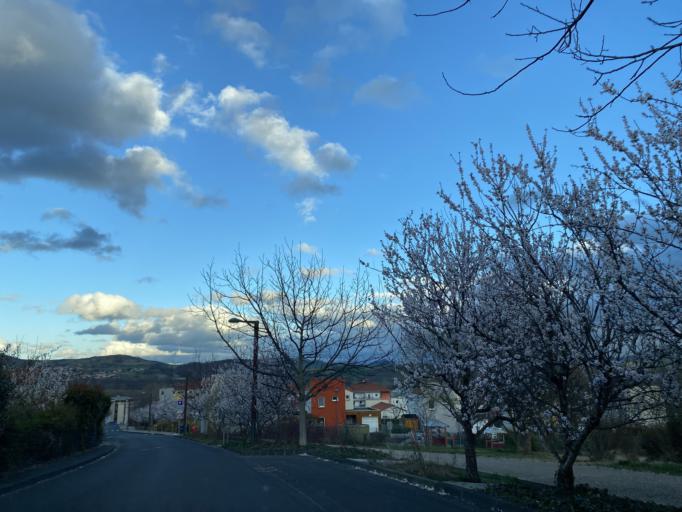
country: FR
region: Auvergne
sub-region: Departement du Puy-de-Dome
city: Cournon-d'Auvergne
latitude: 45.7425
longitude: 3.2062
